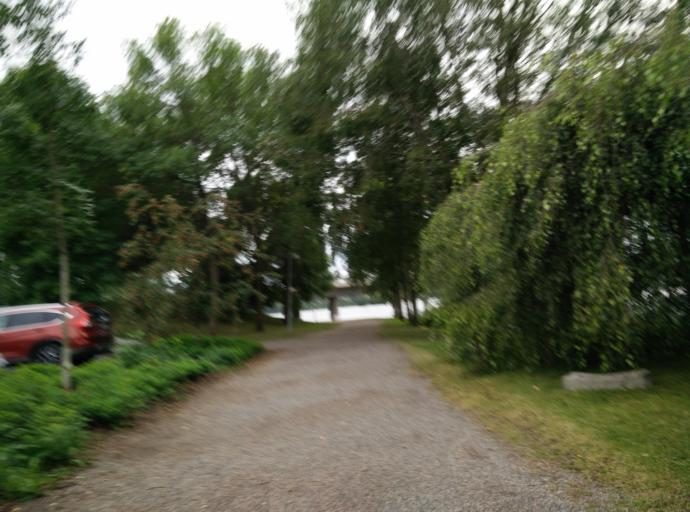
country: FI
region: Haeme
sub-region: Haemeenlinna
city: Haemeenlinna
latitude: 60.9964
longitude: 24.4763
